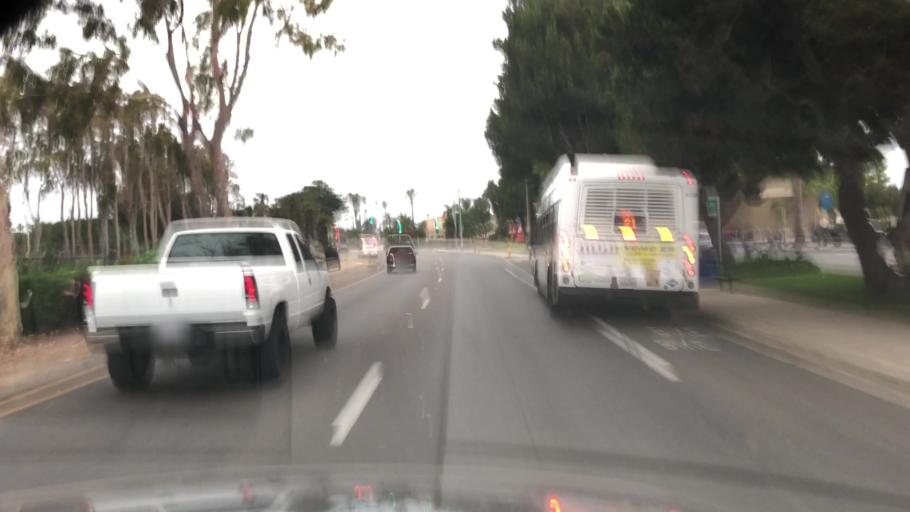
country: US
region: California
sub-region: Ventura County
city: Channel Islands Beach
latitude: 34.1761
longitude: -119.2196
